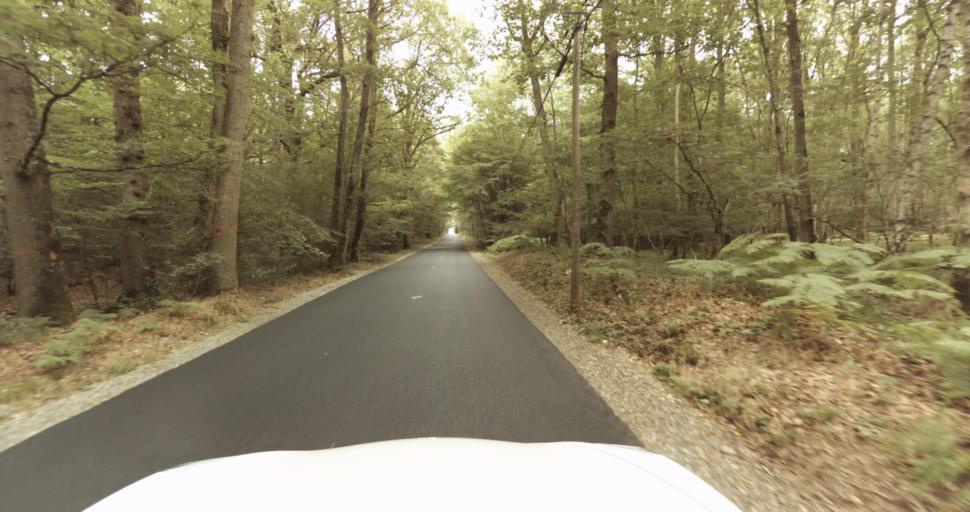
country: FR
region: Haute-Normandie
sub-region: Departement de l'Eure
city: Damville
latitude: 48.9268
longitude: 1.0740
